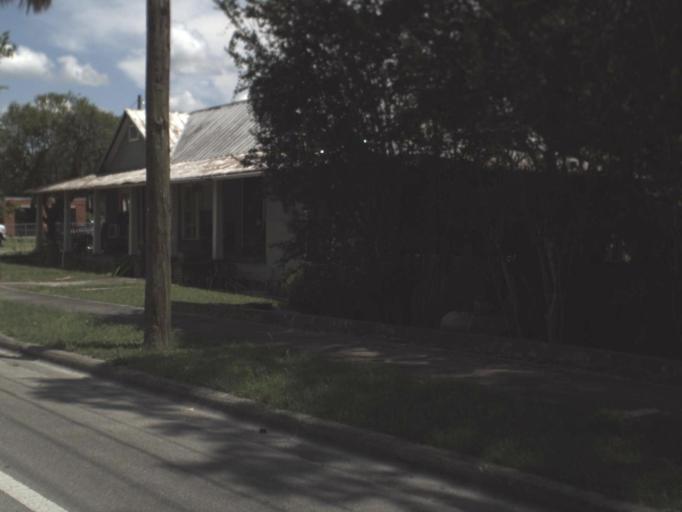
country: US
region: Florida
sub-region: Alachua County
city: High Springs
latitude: 29.8285
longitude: -82.6004
